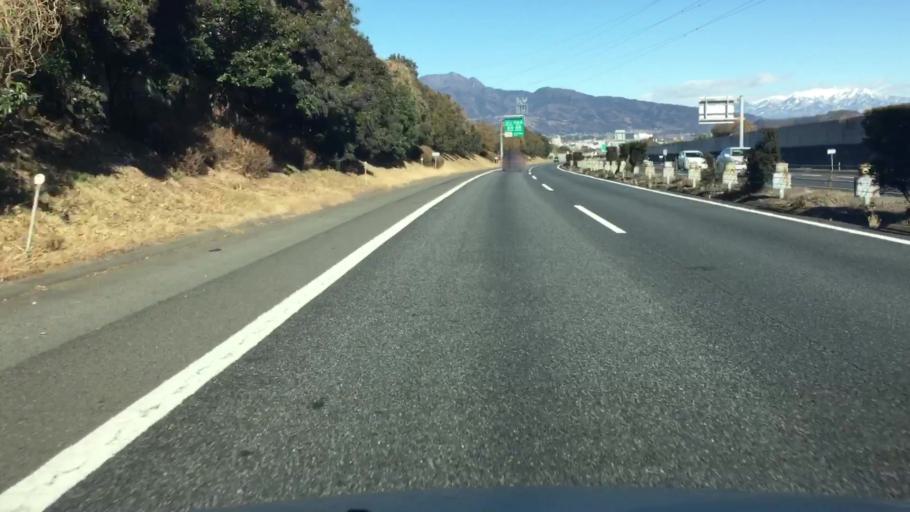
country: JP
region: Gunma
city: Shibukawa
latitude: 36.4640
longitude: 139.0115
